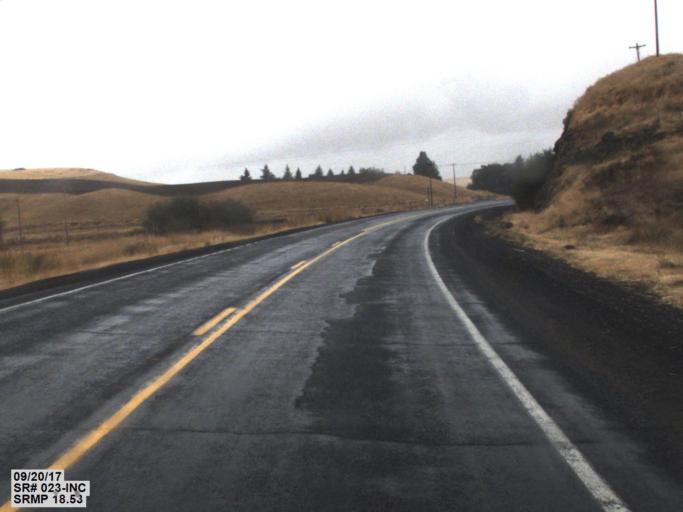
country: US
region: Washington
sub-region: Whitman County
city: Colfax
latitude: 47.1148
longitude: -117.6610
